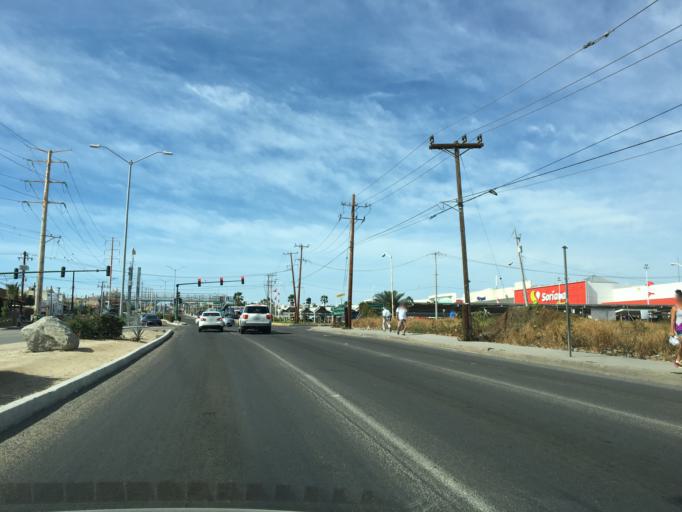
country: MX
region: Baja California Sur
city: Cabo San Lucas
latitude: 22.9024
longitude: -109.9313
